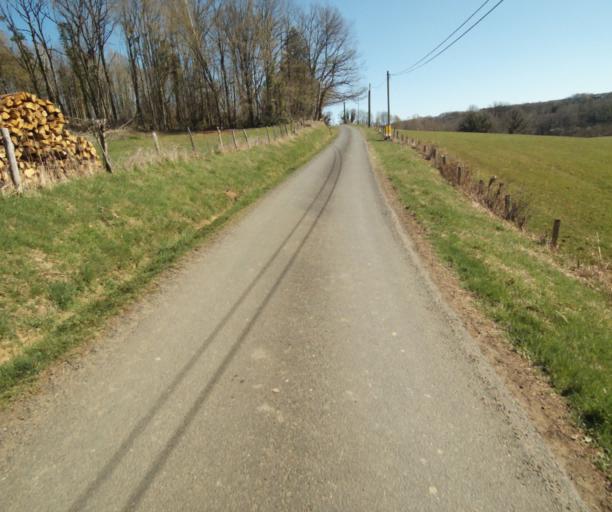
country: FR
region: Limousin
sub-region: Departement de la Correze
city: Chamboulive
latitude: 45.3951
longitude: 1.6568
